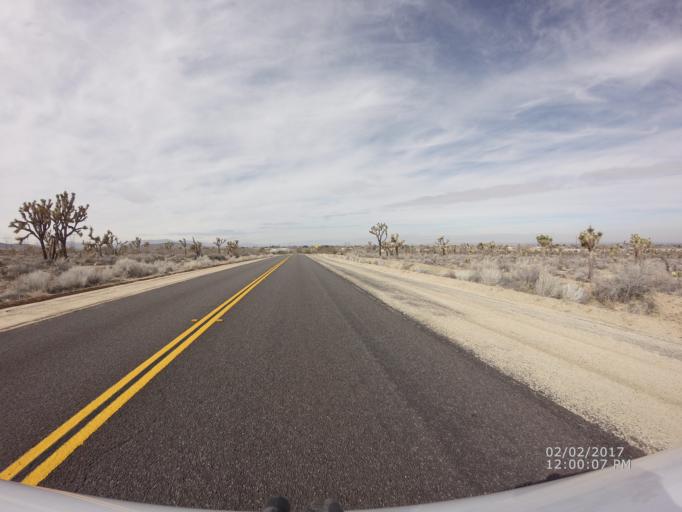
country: US
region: California
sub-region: Los Angeles County
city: Littlerock
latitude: 34.5122
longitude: -117.9781
